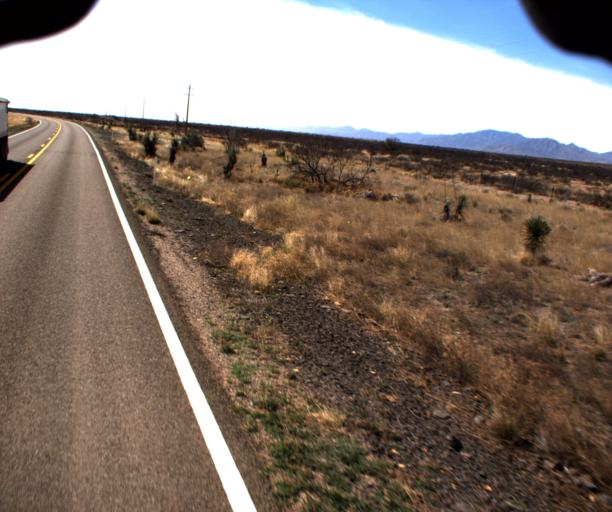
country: US
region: Arizona
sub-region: Cochise County
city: Willcox
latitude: 32.1470
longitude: -109.9345
